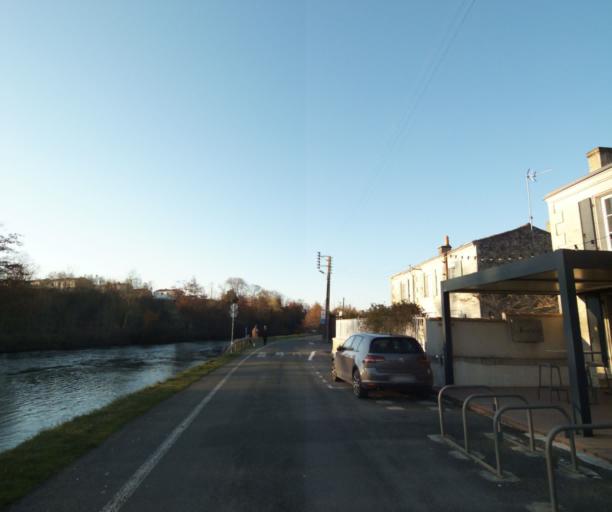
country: FR
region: Poitou-Charentes
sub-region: Departement des Deux-Sevres
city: Niort
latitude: 46.3301
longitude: -0.4780
